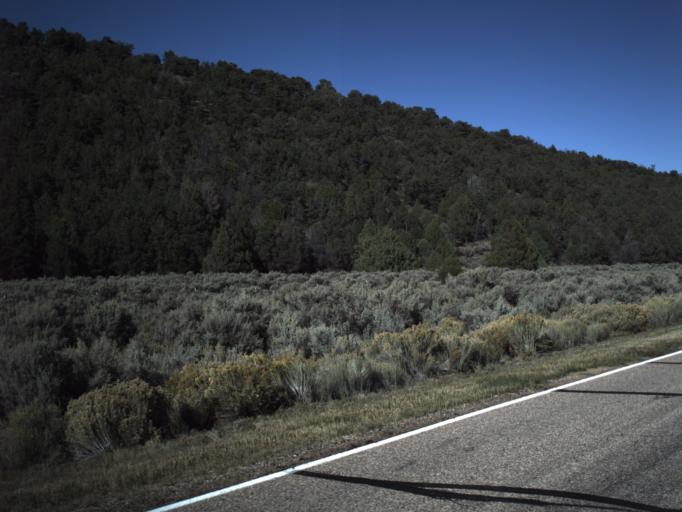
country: US
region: Utah
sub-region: Garfield County
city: Panguitch
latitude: 37.7648
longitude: -112.4965
